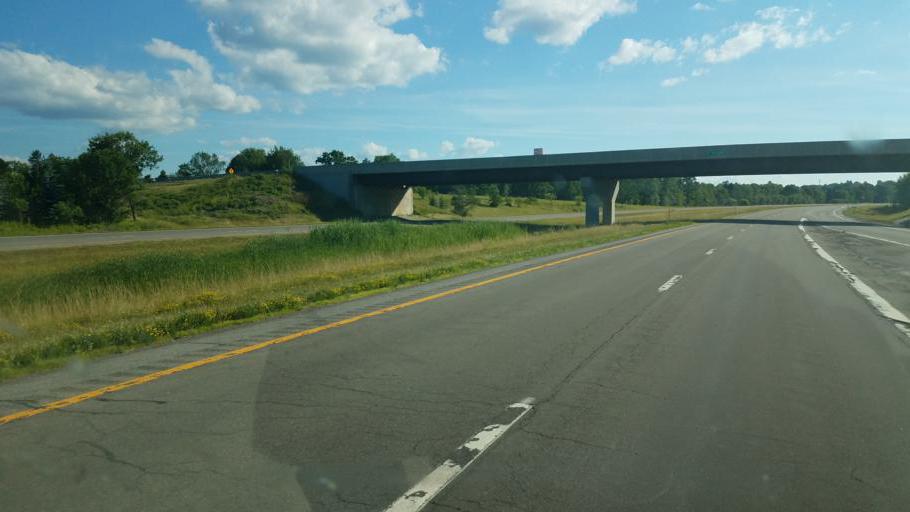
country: US
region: New York
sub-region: Chautauqua County
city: Falconer
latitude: 42.1301
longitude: -79.1901
